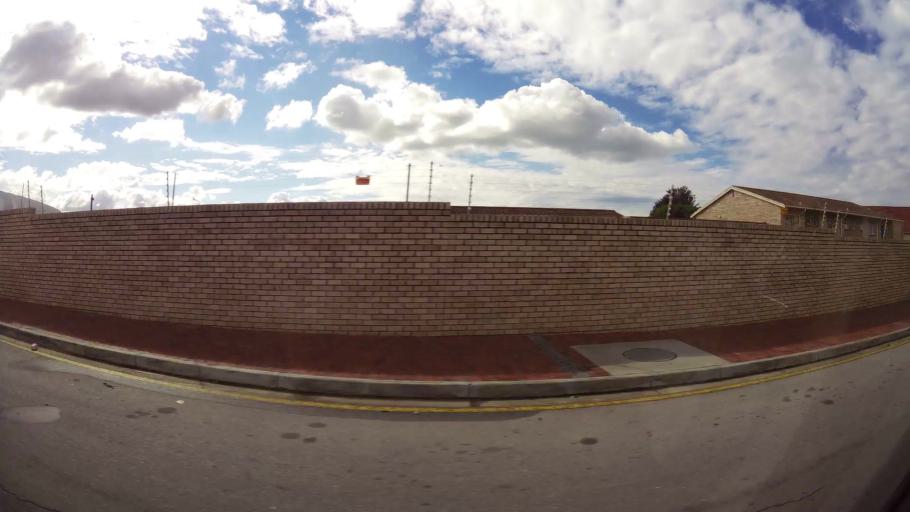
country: ZA
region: Eastern Cape
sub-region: Nelson Mandela Bay Metropolitan Municipality
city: Port Elizabeth
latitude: -33.9417
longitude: 25.6014
